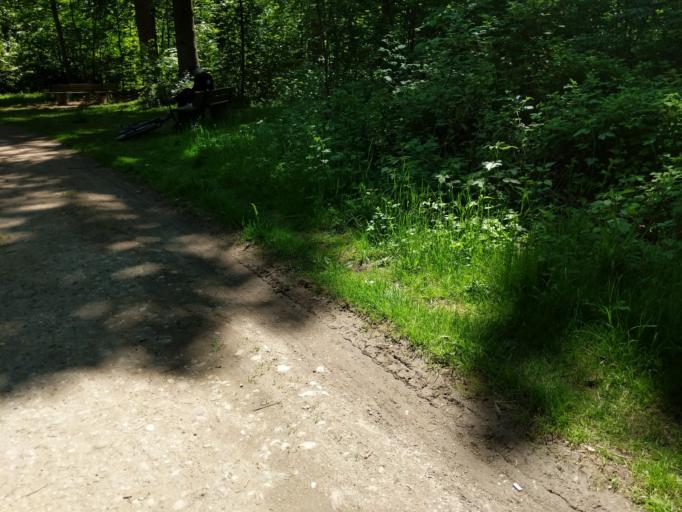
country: DE
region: Bavaria
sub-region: Upper Bavaria
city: Pullach im Isartal
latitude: 48.1015
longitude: 11.5076
